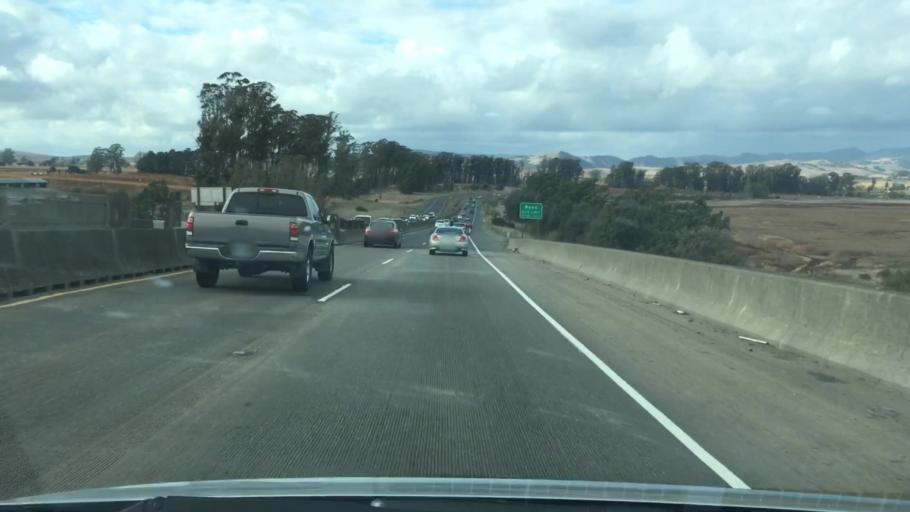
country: US
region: California
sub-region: Napa County
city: Napa
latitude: 38.2451
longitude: -122.2903
